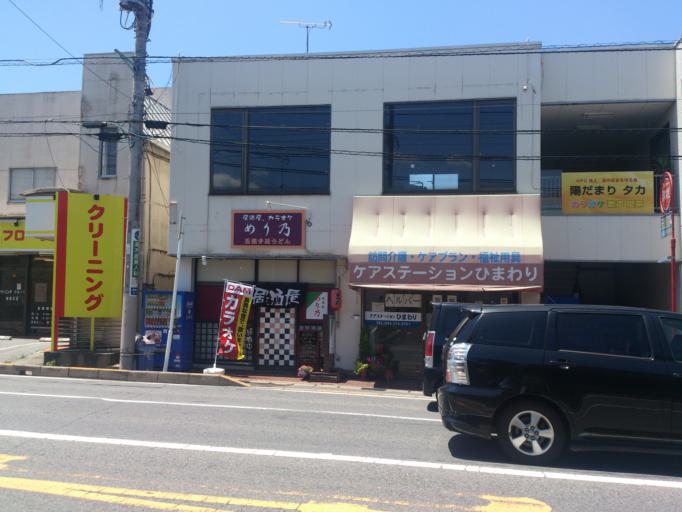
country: JP
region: Chiba
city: Chiba
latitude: 35.6483
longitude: 140.0729
